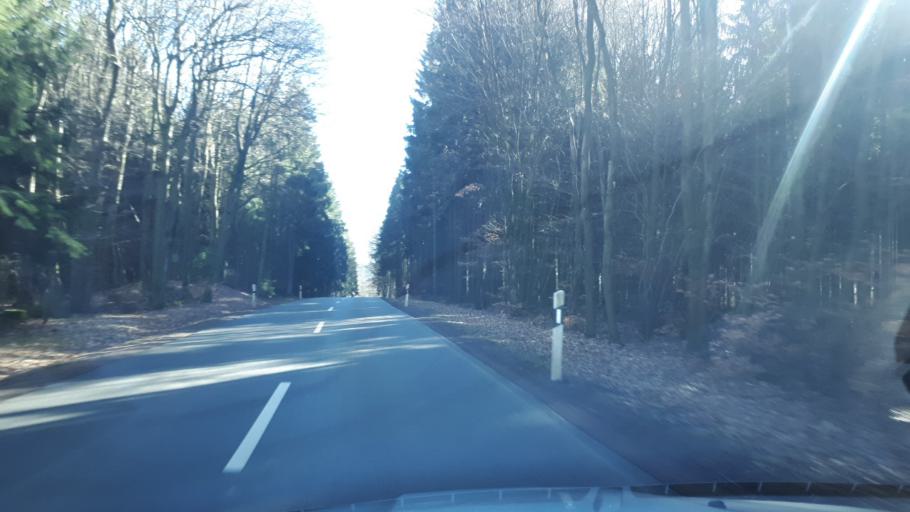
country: DE
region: Rheinland-Pfalz
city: Strohn
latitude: 50.1005
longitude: 6.9140
